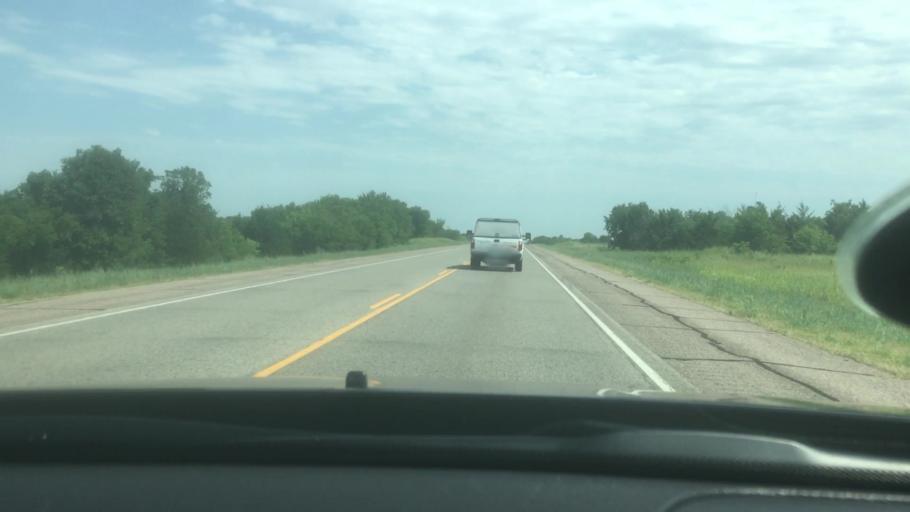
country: US
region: Oklahoma
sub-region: Seminole County
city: Maud
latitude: 35.0392
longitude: -96.9314
